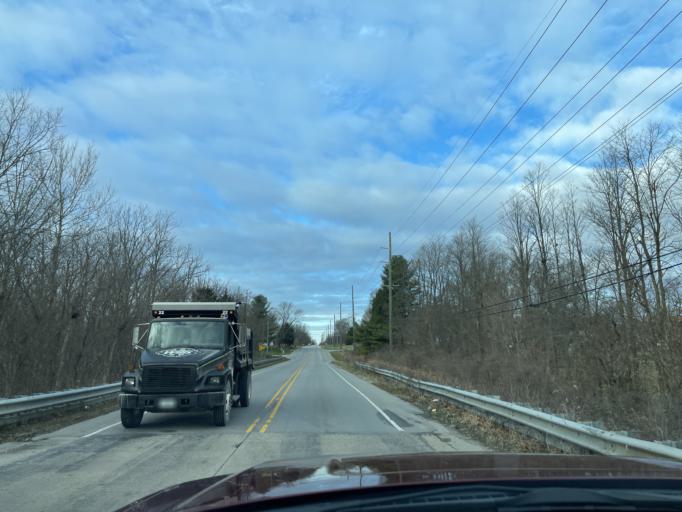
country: US
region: Indiana
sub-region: Hendricks County
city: Avon
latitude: 39.7621
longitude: -86.4452
